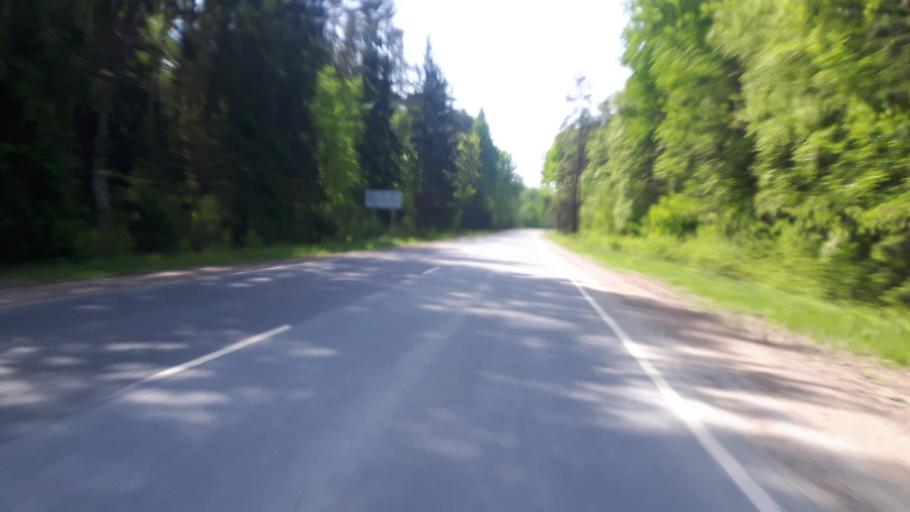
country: RU
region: Leningrad
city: Vistino
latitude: 59.6896
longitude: 28.4613
